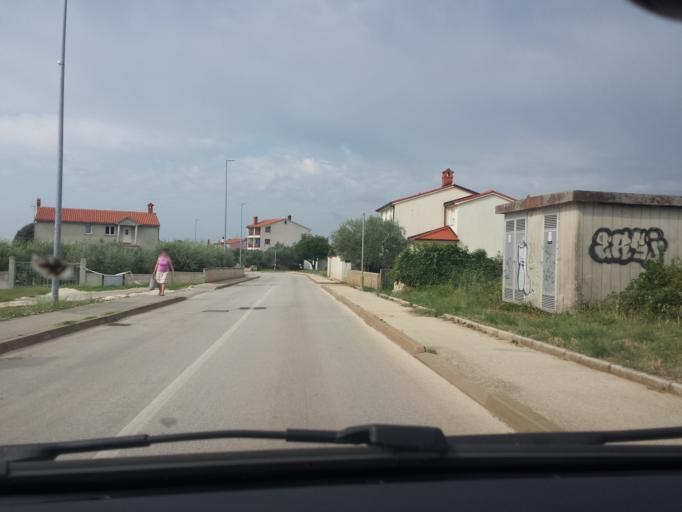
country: HR
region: Istarska
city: Galizana
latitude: 44.9290
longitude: 13.8675
